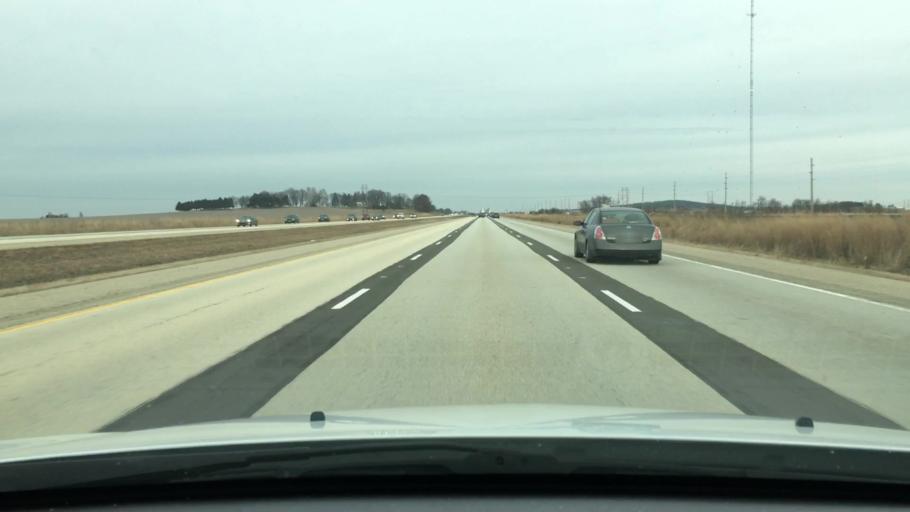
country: US
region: Illinois
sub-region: Sangamon County
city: Williamsville
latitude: 39.9867
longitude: -89.5183
